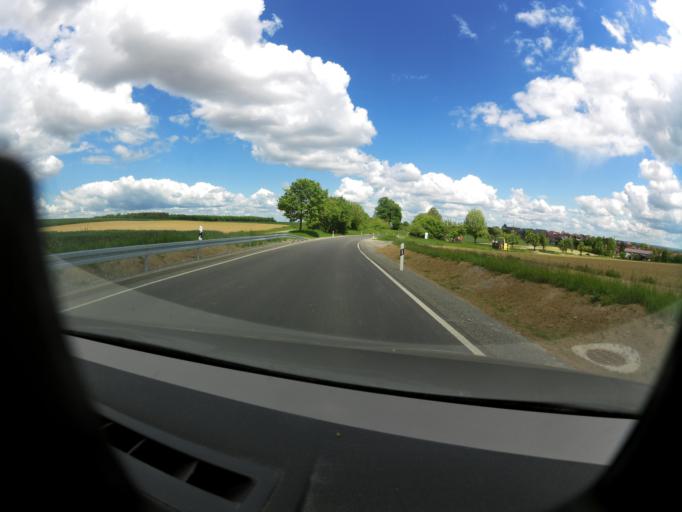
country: DE
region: Bavaria
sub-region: Regierungsbezirk Unterfranken
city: Waigolshausen
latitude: 49.9408
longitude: 10.1399
